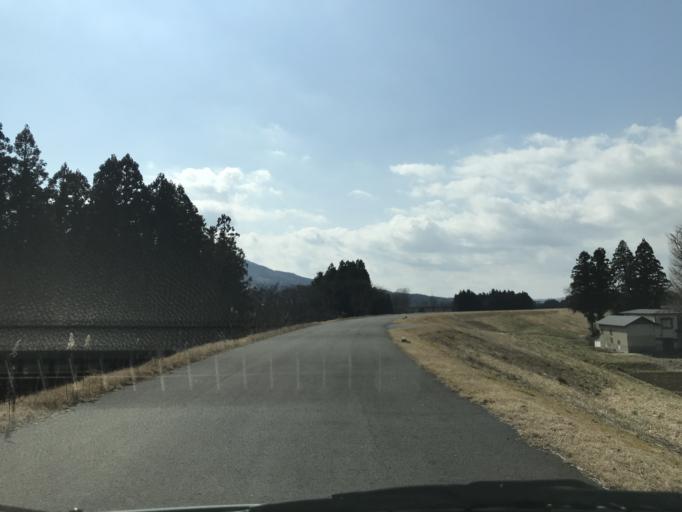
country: JP
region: Iwate
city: Mizusawa
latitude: 39.0475
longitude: 141.1474
